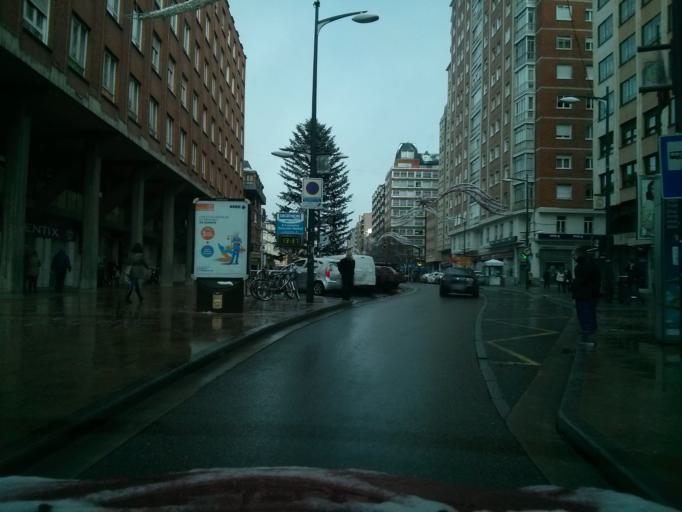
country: ES
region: Castille and Leon
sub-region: Provincia de Burgos
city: Burgos
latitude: 42.3431
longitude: -3.6992
